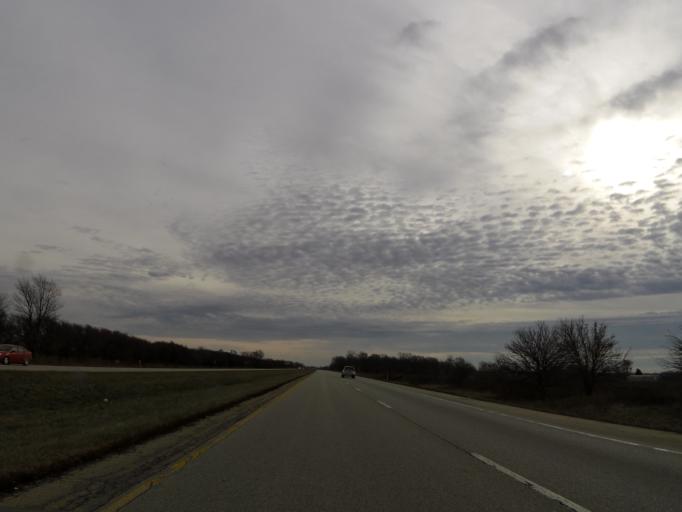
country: US
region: Indiana
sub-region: Boone County
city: Thorntown
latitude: 39.9856
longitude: -86.6946
